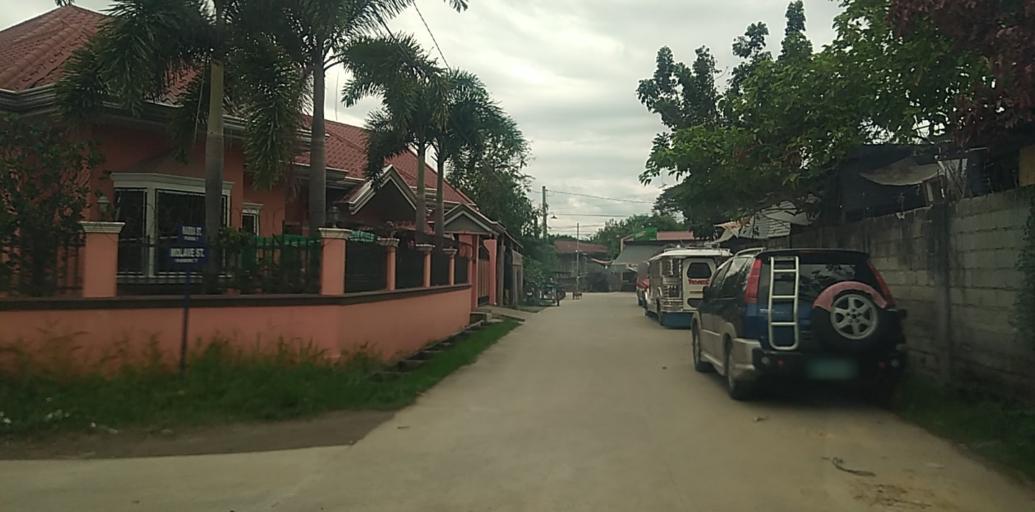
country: PH
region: Central Luzon
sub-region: Province of Pampanga
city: San Fernando
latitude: 15.0021
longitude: 120.7031
